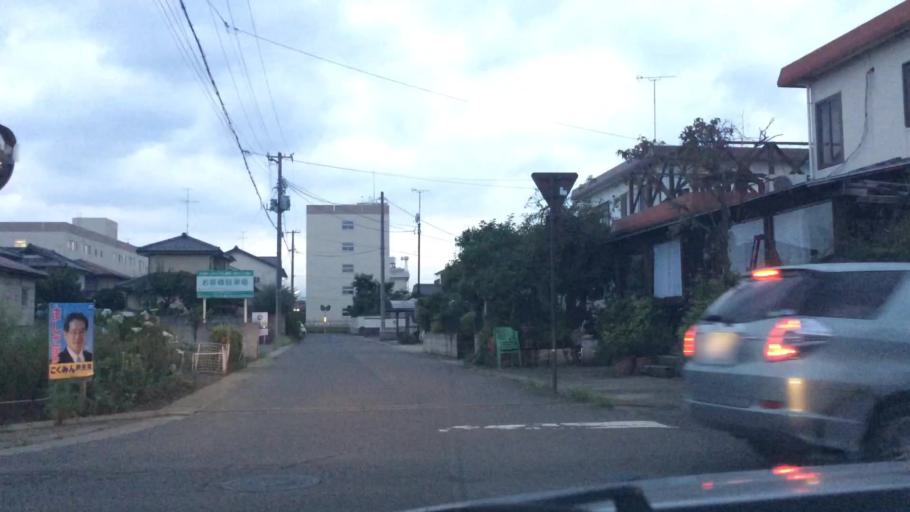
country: JP
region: Fukushima
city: Koriyama
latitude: 37.3922
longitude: 140.3331
